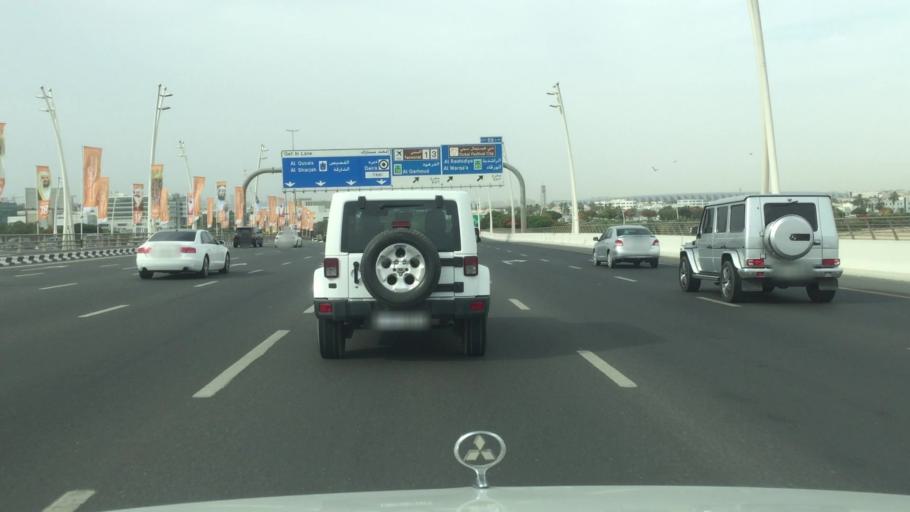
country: AE
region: Ash Shariqah
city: Sharjah
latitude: 25.2343
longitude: 55.3390
